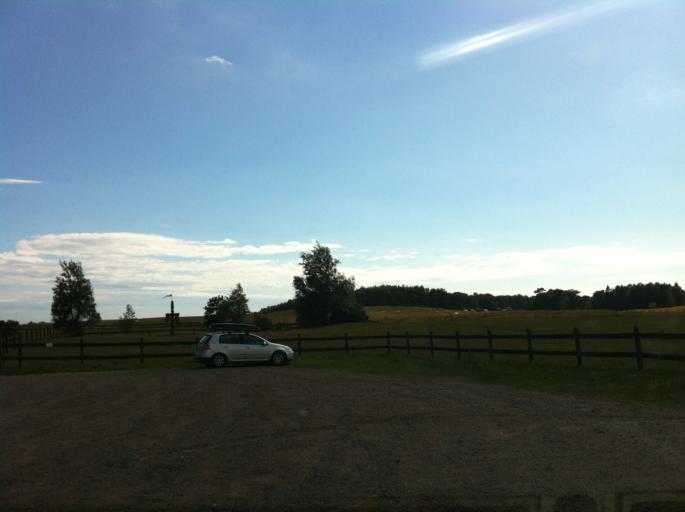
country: SE
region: Skane
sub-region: Ystads Kommun
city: Kopingebro
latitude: 55.3902
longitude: 14.0551
